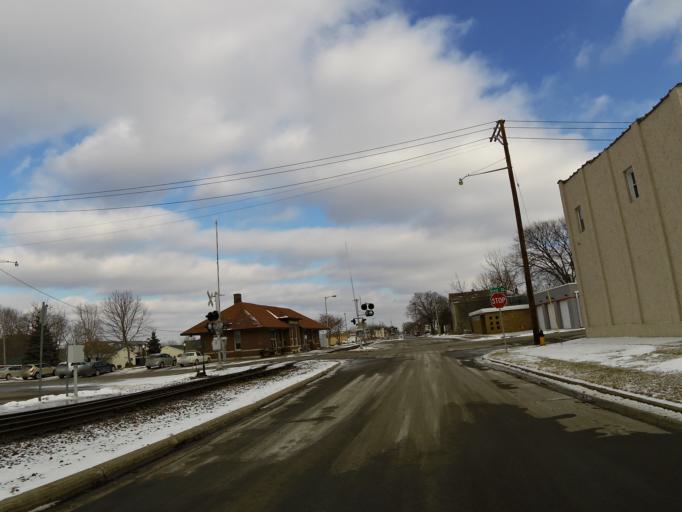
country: US
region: Minnesota
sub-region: Scott County
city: Shakopee
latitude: 44.7969
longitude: -93.5313
